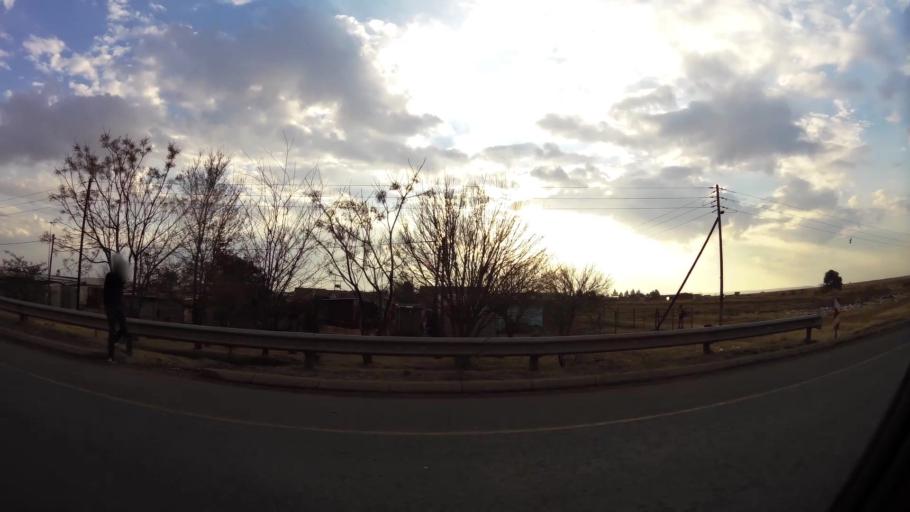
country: ZA
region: Gauteng
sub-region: Sedibeng District Municipality
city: Vanderbijlpark
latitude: -26.6036
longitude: 27.8175
